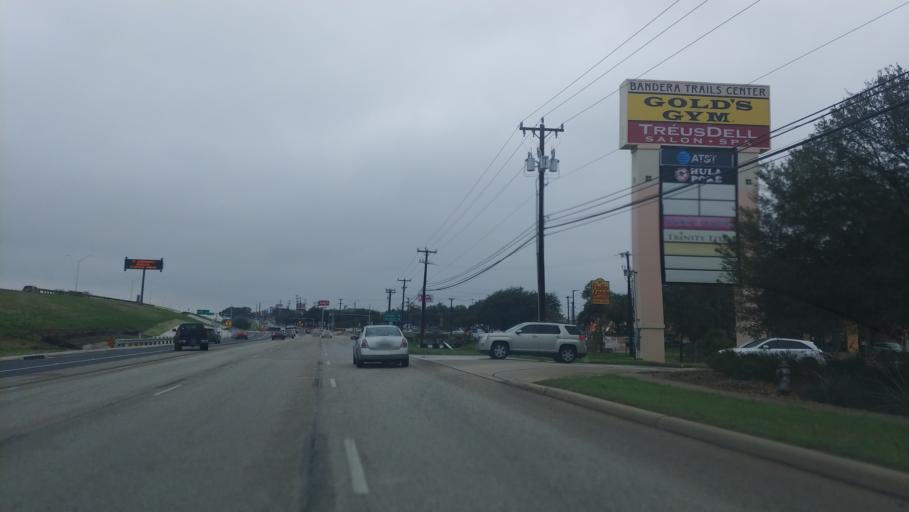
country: US
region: Texas
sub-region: Bexar County
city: Helotes
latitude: 29.5562
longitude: -98.6653
